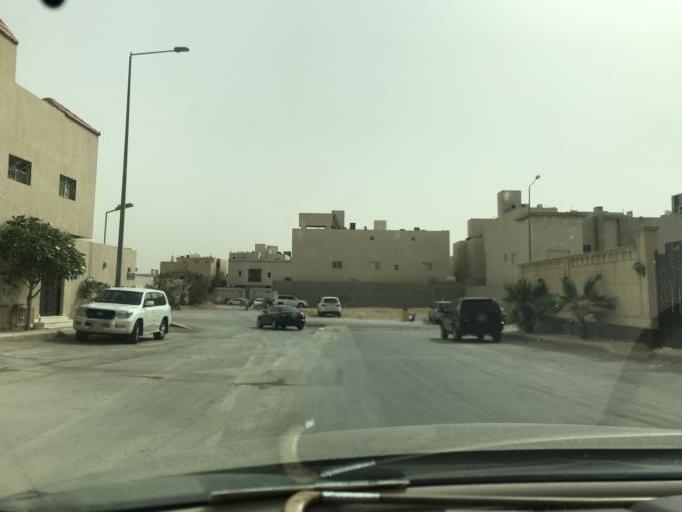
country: SA
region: Ar Riyad
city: Riyadh
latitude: 24.8185
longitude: 46.5990
